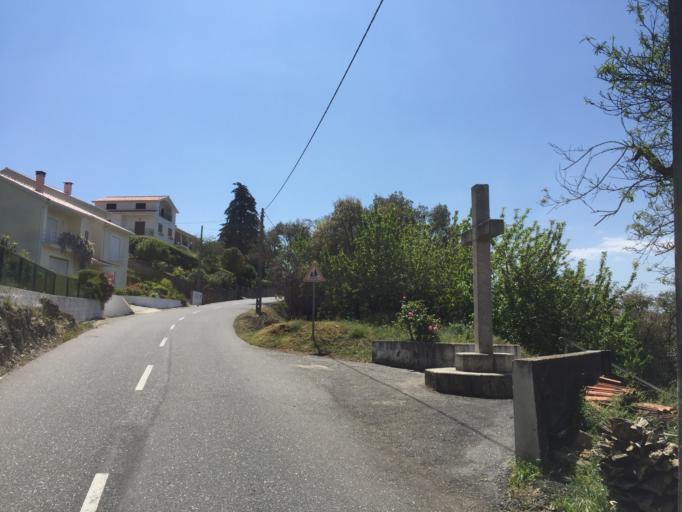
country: PT
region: Coimbra
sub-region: Pampilhosa da Serra
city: Pampilhosa da Serra
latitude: 40.0899
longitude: -7.8785
